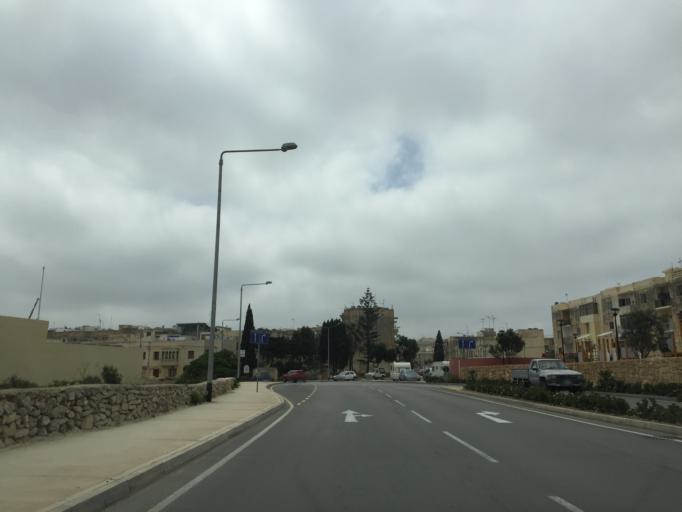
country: MT
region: Ir-Rabat
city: Rabat
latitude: 35.8845
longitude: 14.3910
